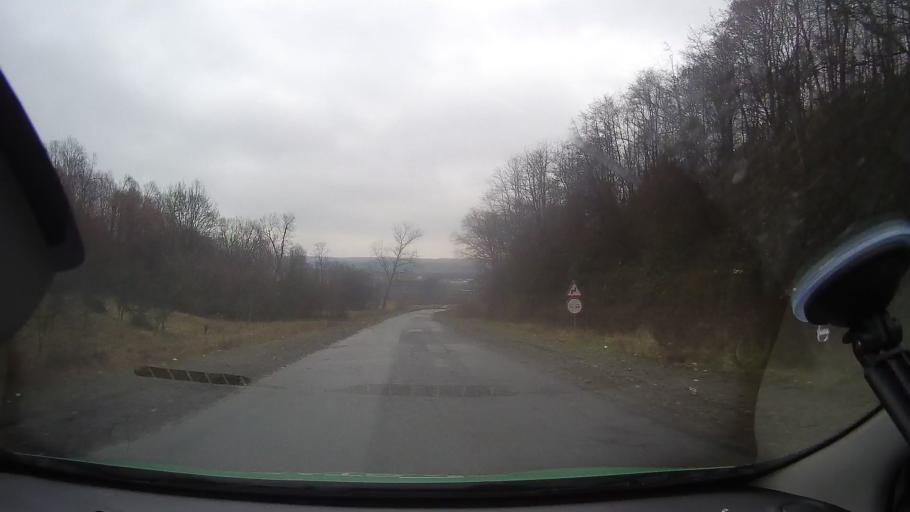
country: RO
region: Arad
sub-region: Comuna Halmagiu
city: Halmagiu
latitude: 46.2780
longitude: 22.5914
